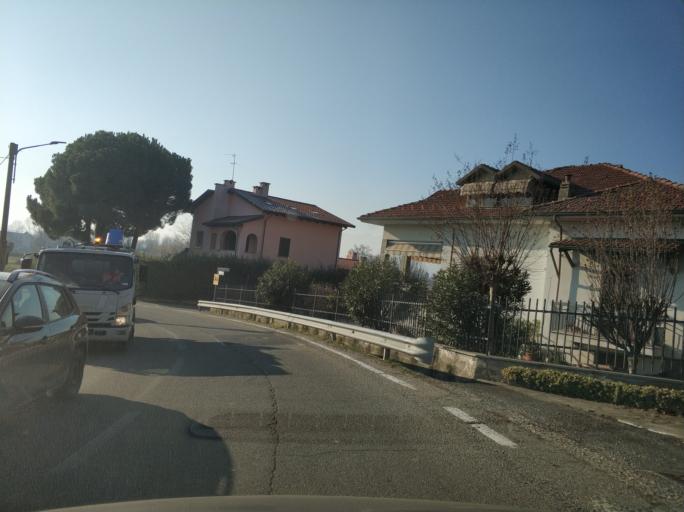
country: IT
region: Piedmont
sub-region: Provincia di Torino
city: Nole
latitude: 45.2561
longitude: 7.5767
